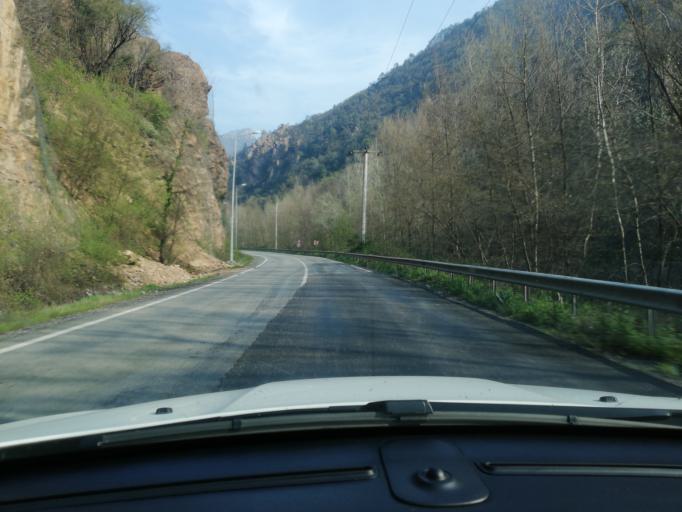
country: TR
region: Karabuk
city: Yenice
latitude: 41.1813
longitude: 32.4483
